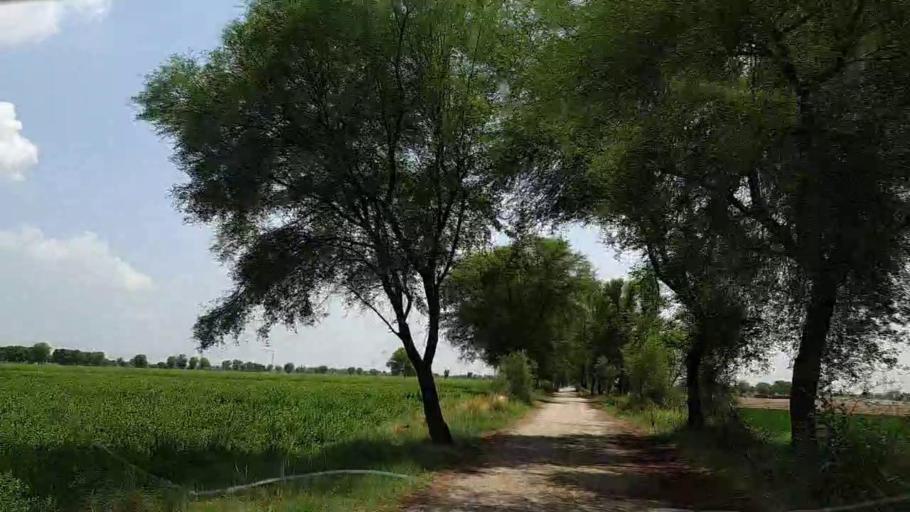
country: PK
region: Sindh
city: Tharu Shah
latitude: 27.0158
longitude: 68.0701
